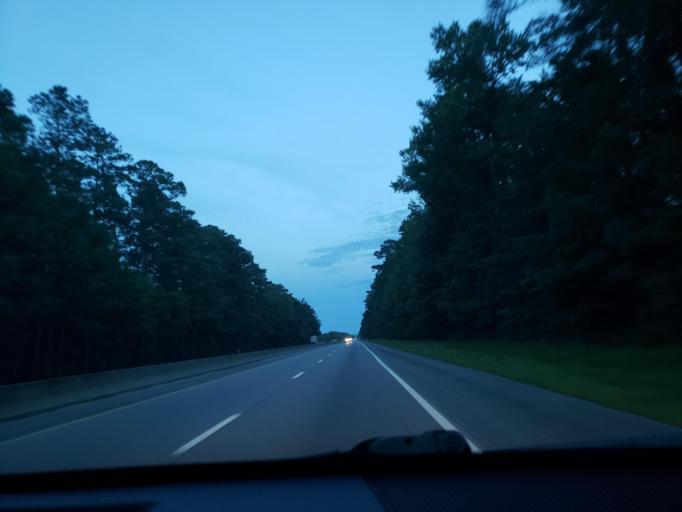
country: US
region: Virginia
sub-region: City of Franklin
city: Franklin
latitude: 36.6580
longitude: -76.9329
